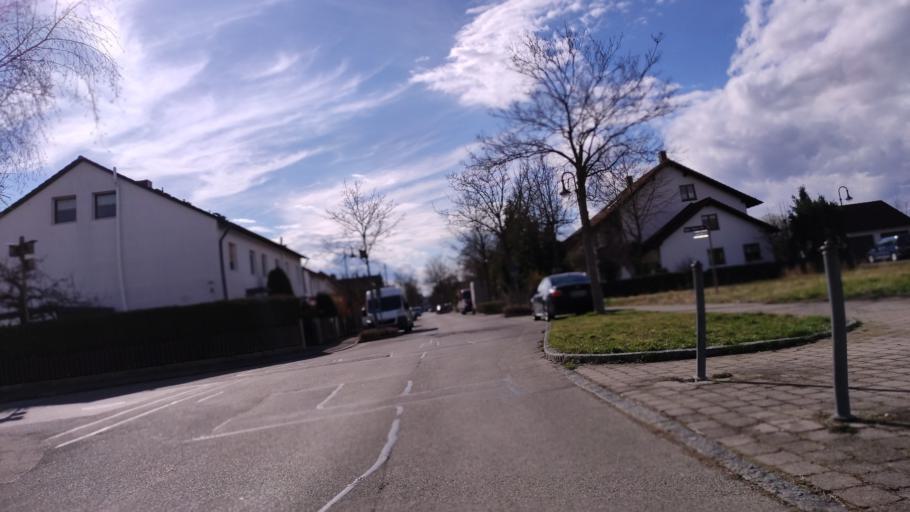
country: DE
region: Bavaria
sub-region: Upper Bavaria
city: Emmering
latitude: 48.1901
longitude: 11.2786
